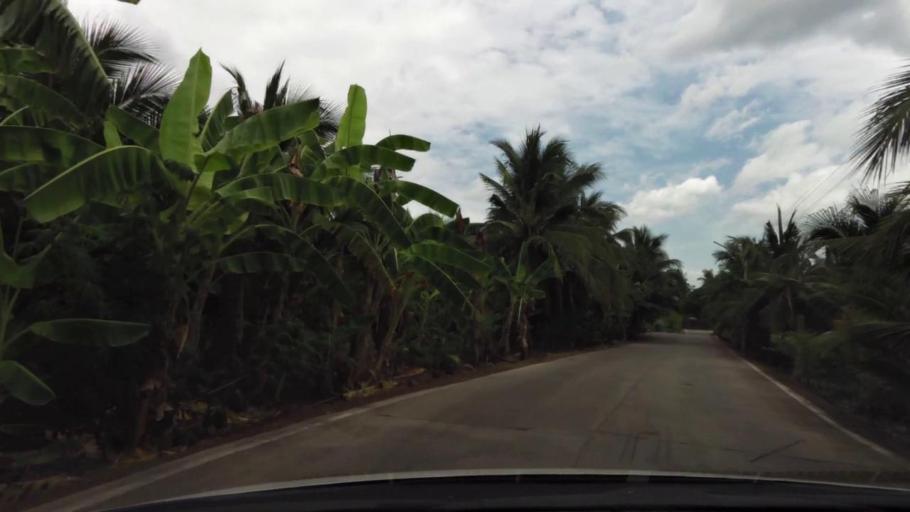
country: TH
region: Samut Sakhon
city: Ban Phaeo
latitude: 13.5657
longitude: 100.0359
